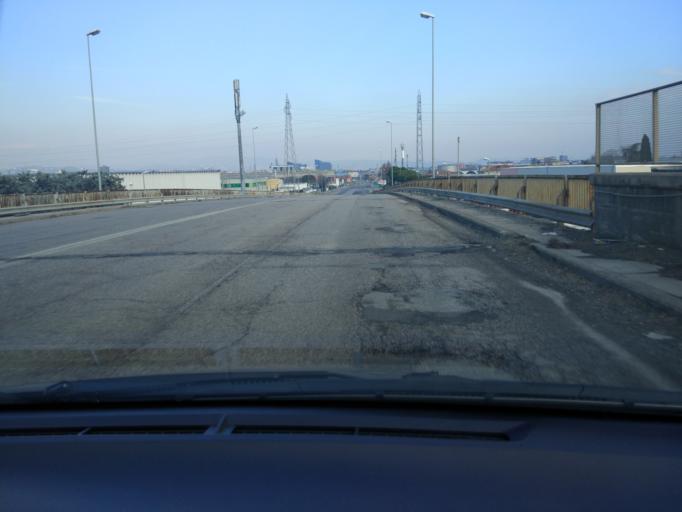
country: IT
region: Veneto
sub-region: Provincia di Verona
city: Beccacivetta-Azzano
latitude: 45.4045
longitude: 10.9547
